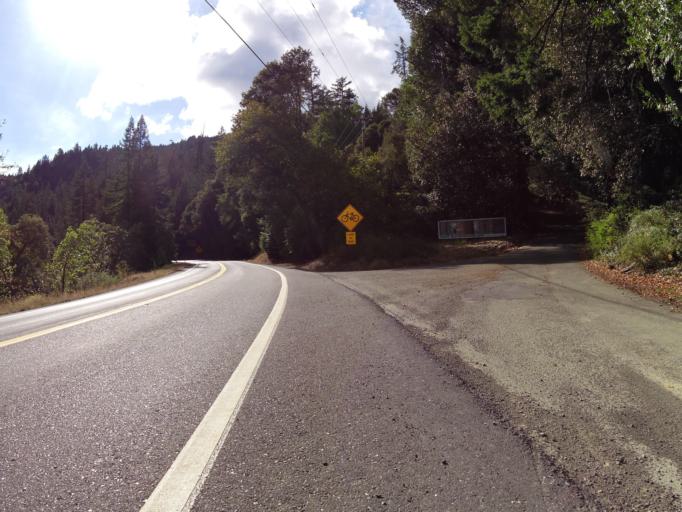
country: US
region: California
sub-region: Humboldt County
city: Redway
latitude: 40.0356
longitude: -123.7900
